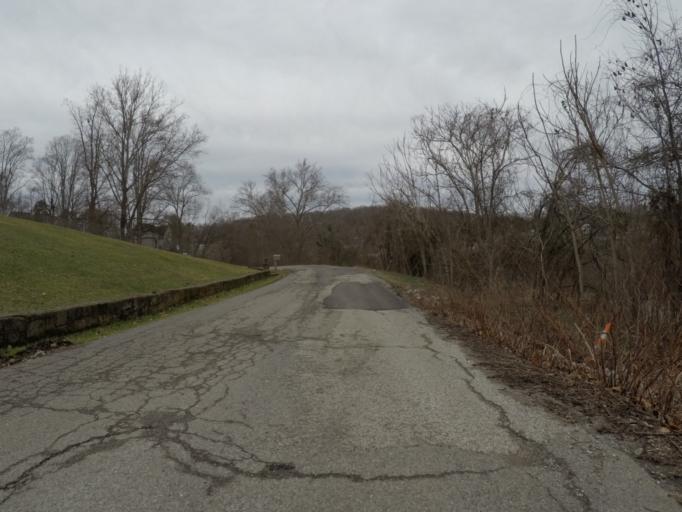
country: US
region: Ohio
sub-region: Lawrence County
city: Burlington
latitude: 38.3816
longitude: -82.5145
